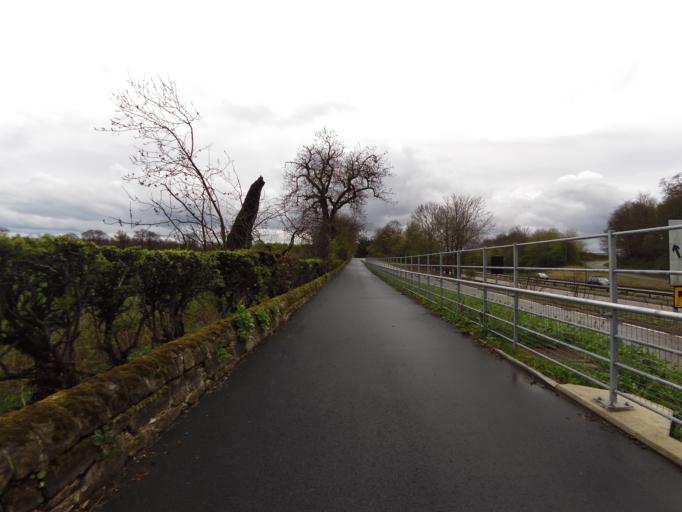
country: GB
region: Scotland
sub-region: Edinburgh
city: Queensferry
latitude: 55.9729
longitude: -3.3310
